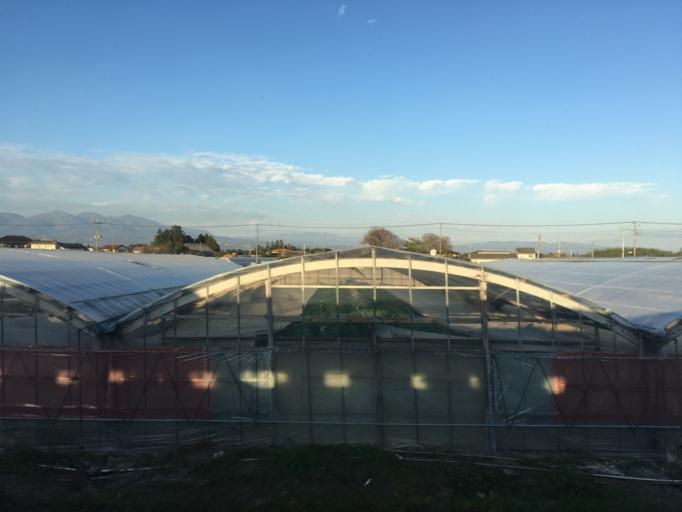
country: JP
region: Gunma
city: Isesaki
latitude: 36.3456
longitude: 139.1601
